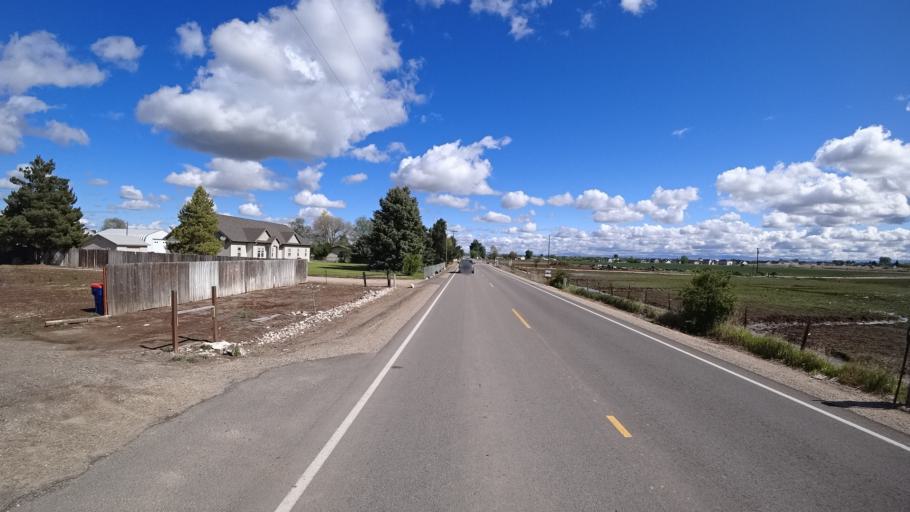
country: US
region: Idaho
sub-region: Ada County
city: Kuna
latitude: 43.4986
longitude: -116.4537
